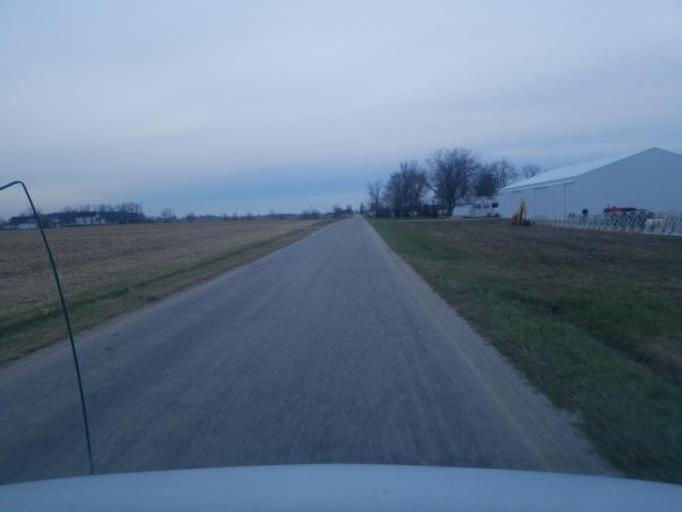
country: US
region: Indiana
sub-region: Adams County
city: Decatur
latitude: 40.7422
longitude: -84.8796
